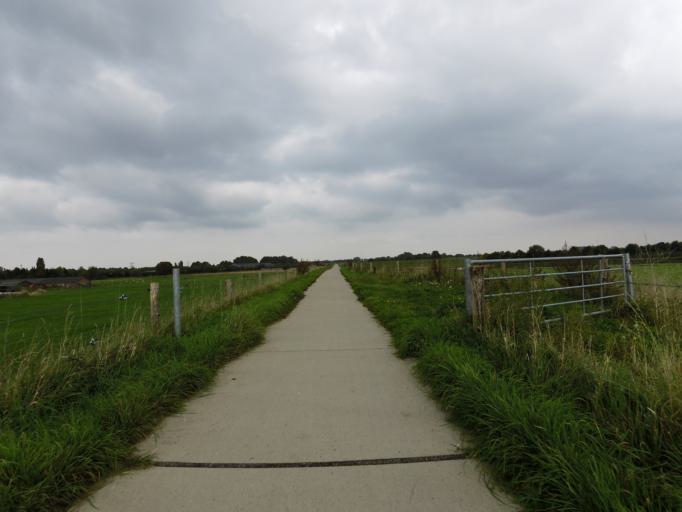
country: NL
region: Gelderland
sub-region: Gemeente Duiven
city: Duiven
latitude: 51.9189
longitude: 6.0111
